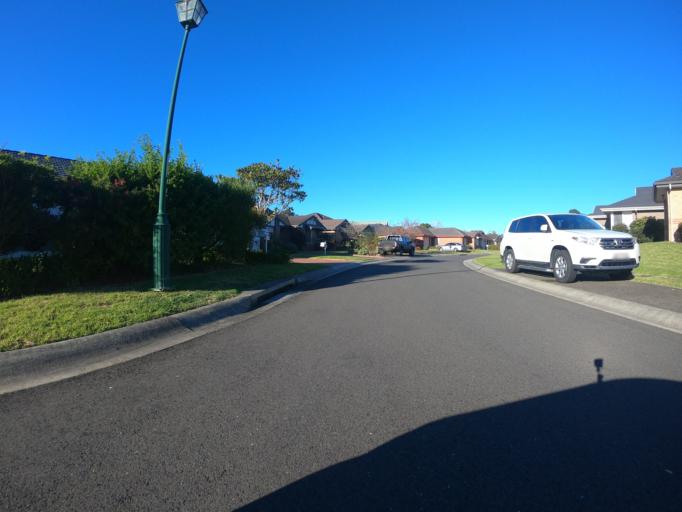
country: AU
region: New South Wales
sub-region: Wollongong
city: Bulli
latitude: -34.3386
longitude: 150.9083
